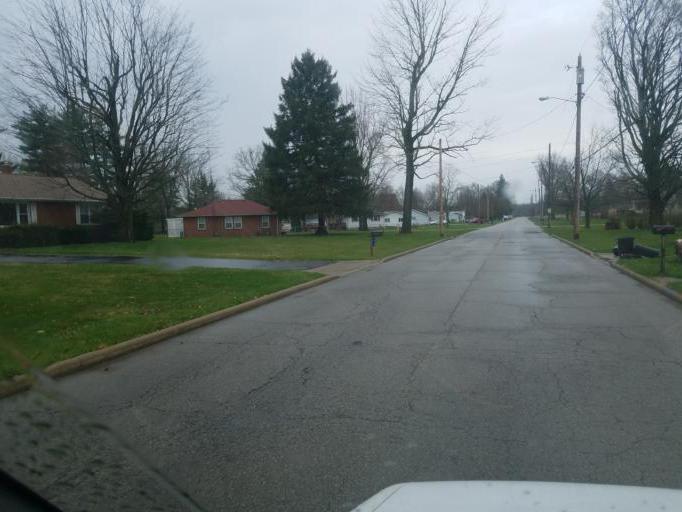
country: US
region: Ohio
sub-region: Crawford County
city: Galion
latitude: 40.7199
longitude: -82.7913
